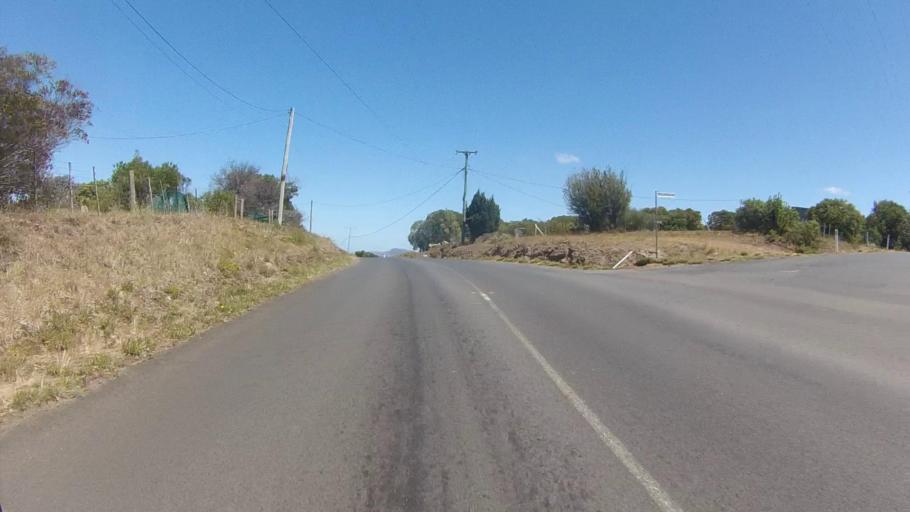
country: AU
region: Tasmania
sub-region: Sorell
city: Sorell
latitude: -42.7743
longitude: 147.5673
